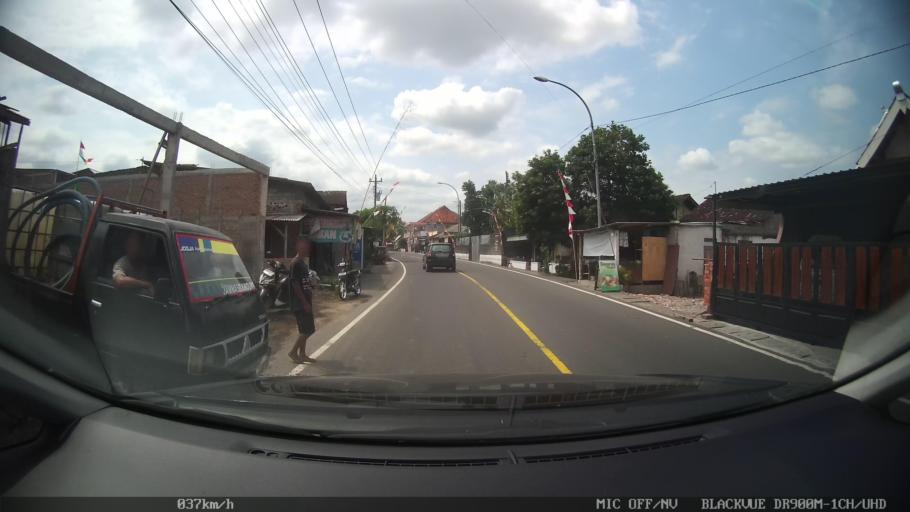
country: ID
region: Central Java
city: Candi Prambanan
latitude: -7.7381
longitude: 110.4820
